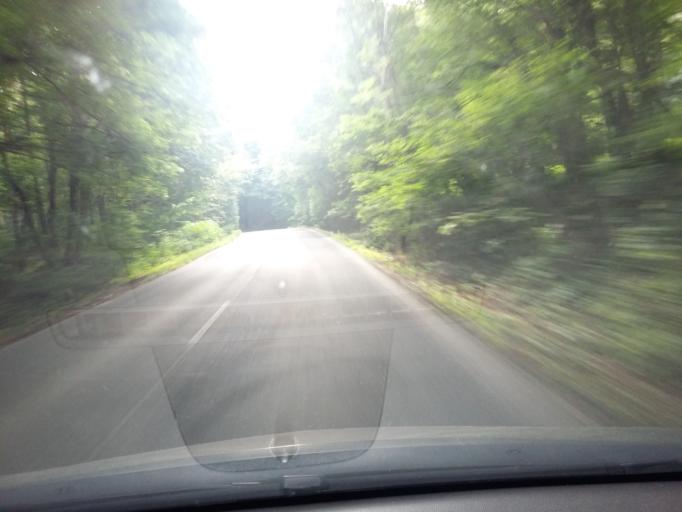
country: SK
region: Trnavsky
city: Smolenice
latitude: 48.5397
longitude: 17.3453
